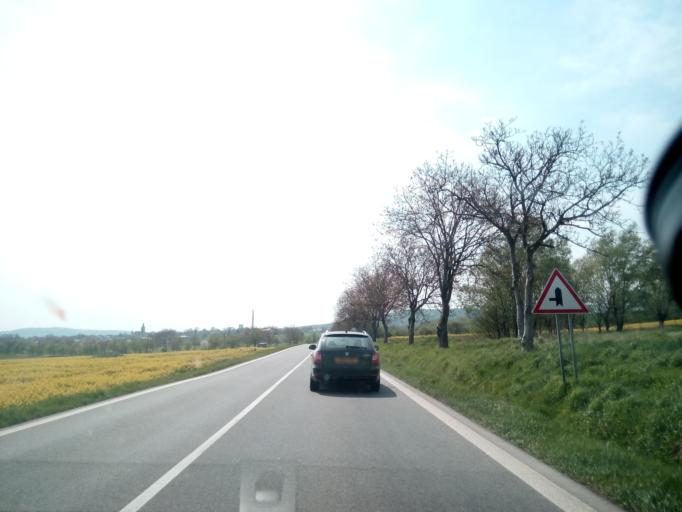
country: SK
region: Presovsky
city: Giraltovce
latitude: 49.0204
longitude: 21.5318
